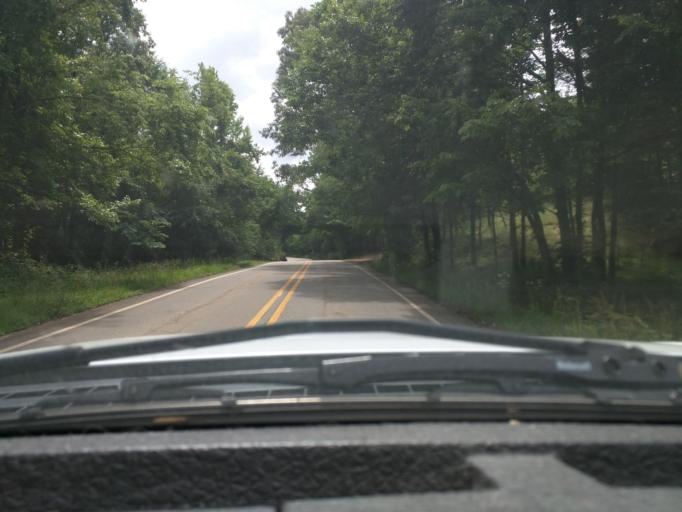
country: US
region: Arkansas
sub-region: Franklin County
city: Ozark
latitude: 35.6841
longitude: -93.8236
